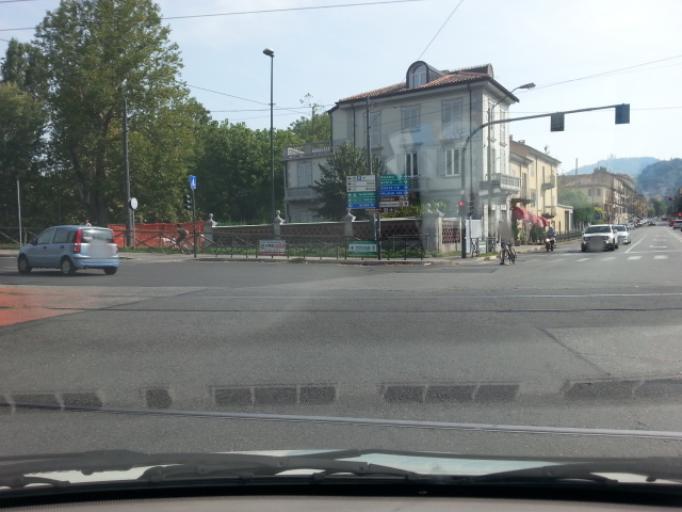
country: IT
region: Piedmont
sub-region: Provincia di Torino
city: Turin
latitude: 45.0672
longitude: 7.7088
